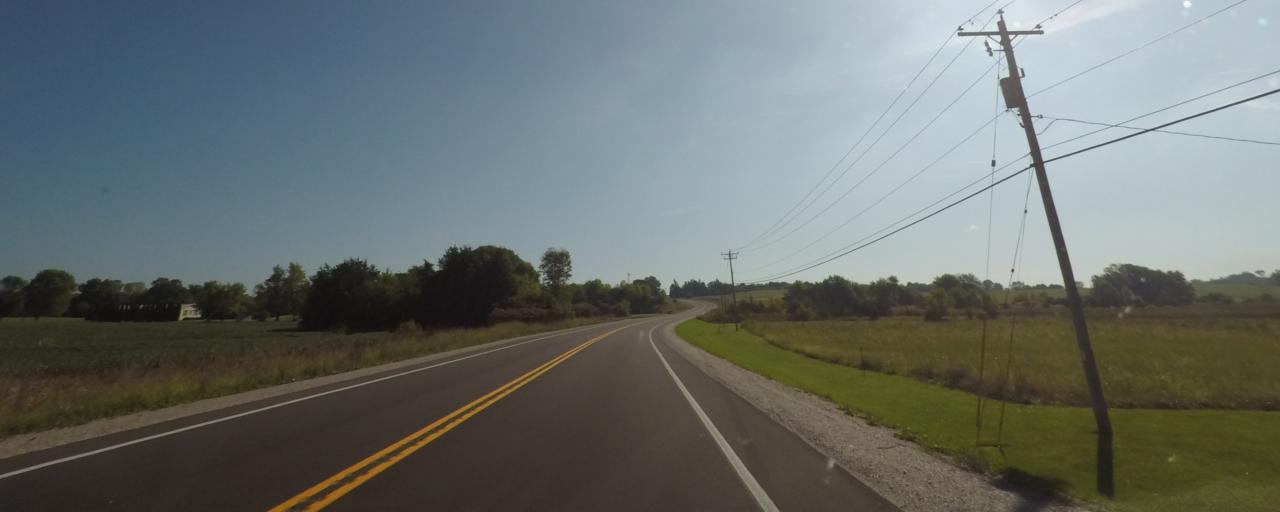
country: US
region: Wisconsin
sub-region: Jefferson County
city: Johnson Creek
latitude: 43.0182
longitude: -88.7287
